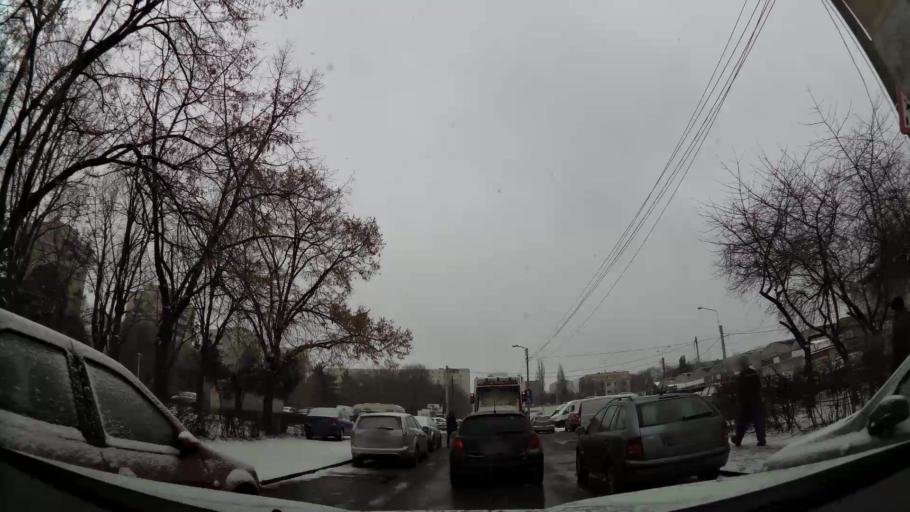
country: RO
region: Prahova
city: Ploiesti
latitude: 44.9340
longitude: 25.9865
